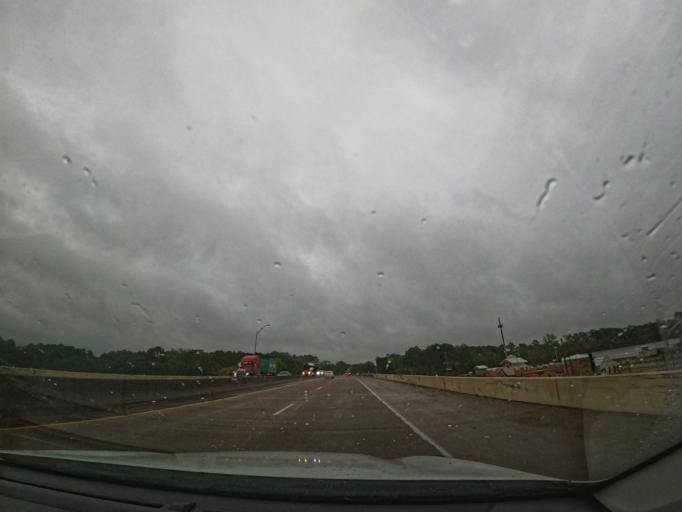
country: US
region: Texas
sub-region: Angelina County
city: Lufkin
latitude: 31.3188
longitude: -94.6996
